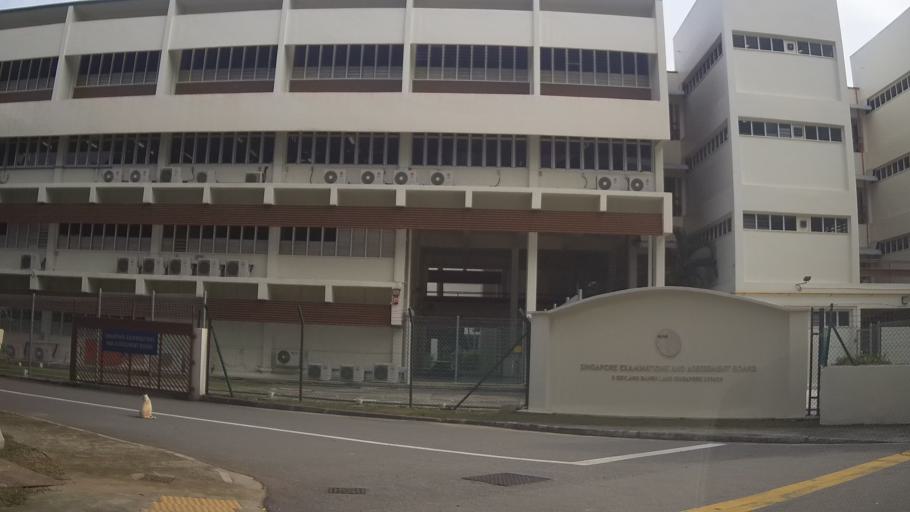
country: SG
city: Singapore
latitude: 1.3241
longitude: 103.8701
